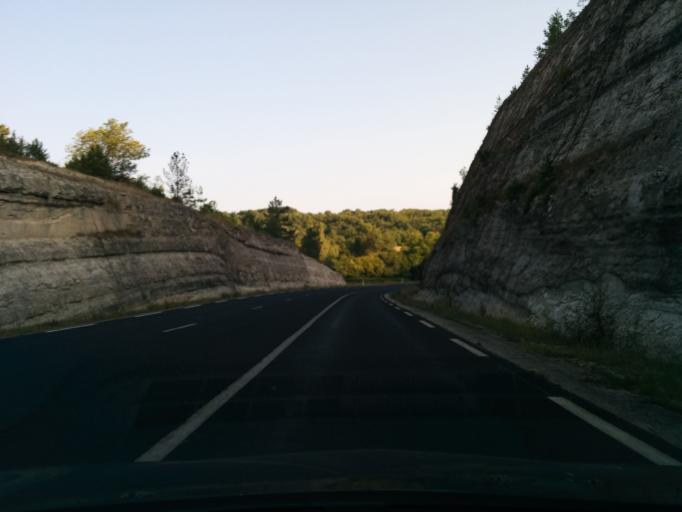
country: FR
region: Midi-Pyrenees
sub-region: Departement du Lot
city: Le Vigan
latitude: 44.7116
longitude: 1.4835
